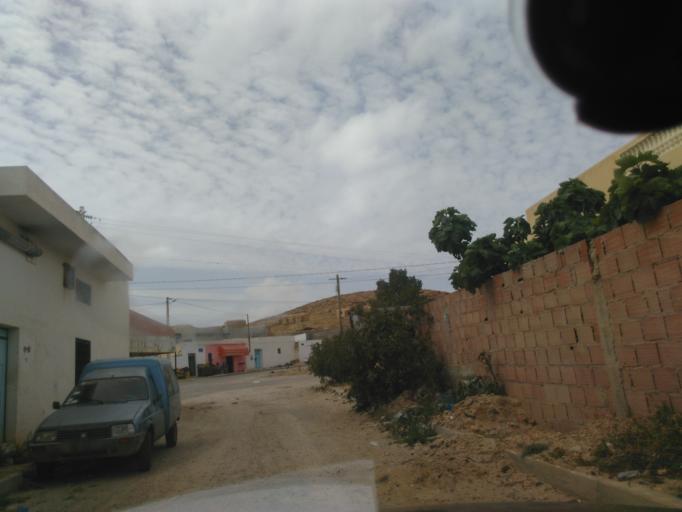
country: TN
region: Tataouine
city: Tataouine
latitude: 32.9455
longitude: 10.4695
